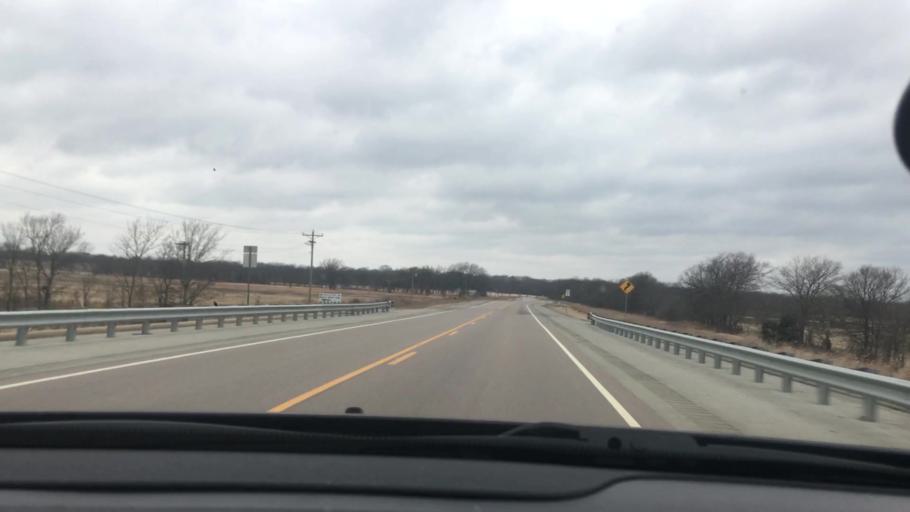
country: US
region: Oklahoma
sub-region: Atoka County
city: Atoka
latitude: 34.3692
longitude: -96.3225
